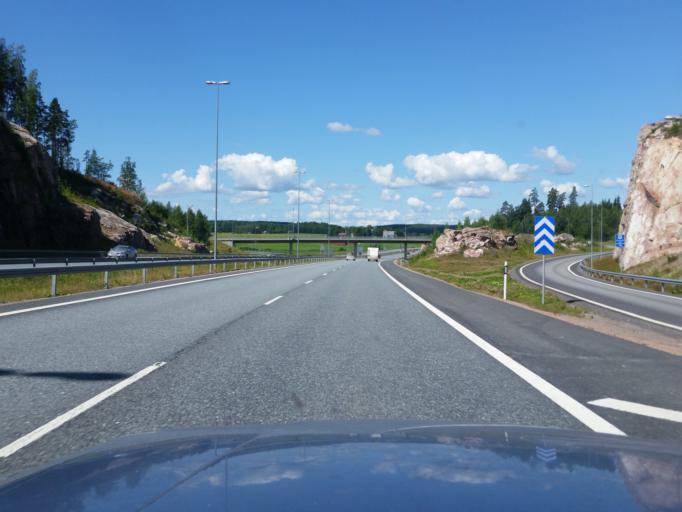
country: FI
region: Varsinais-Suomi
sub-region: Salo
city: Muurla
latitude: 60.3783
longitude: 23.3248
